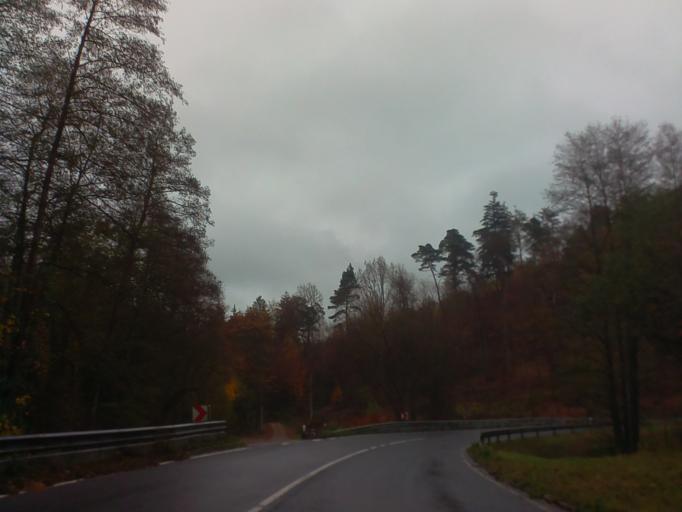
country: DE
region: Baden-Wuerttemberg
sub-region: Karlsruhe Region
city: Wilhelmsfeld
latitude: 49.4742
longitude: 8.7154
